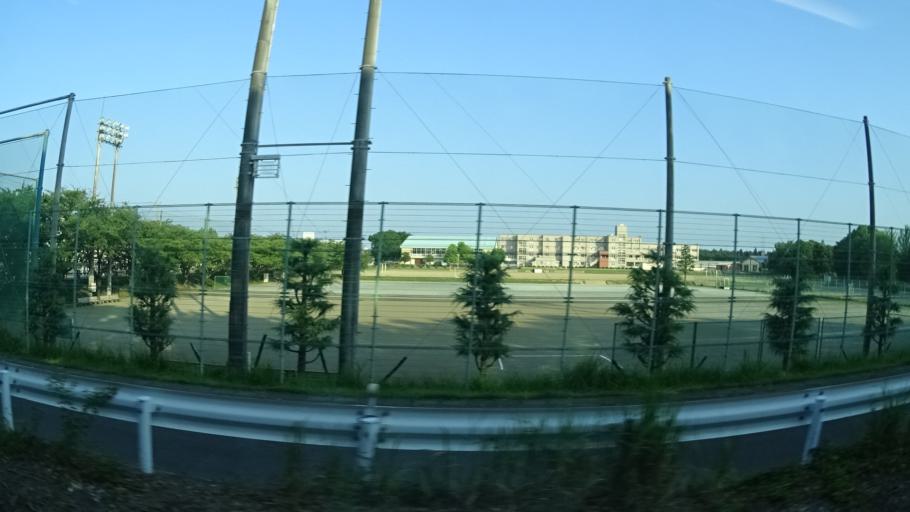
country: JP
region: Ibaraki
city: Funaishikawa
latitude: 36.4601
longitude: 140.5591
